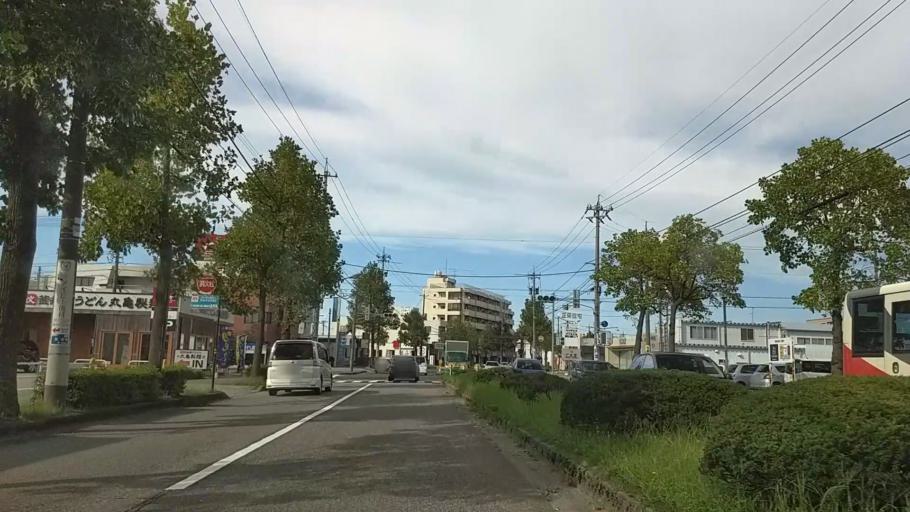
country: JP
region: Ishikawa
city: Nonoichi
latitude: 36.5410
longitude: 136.6394
